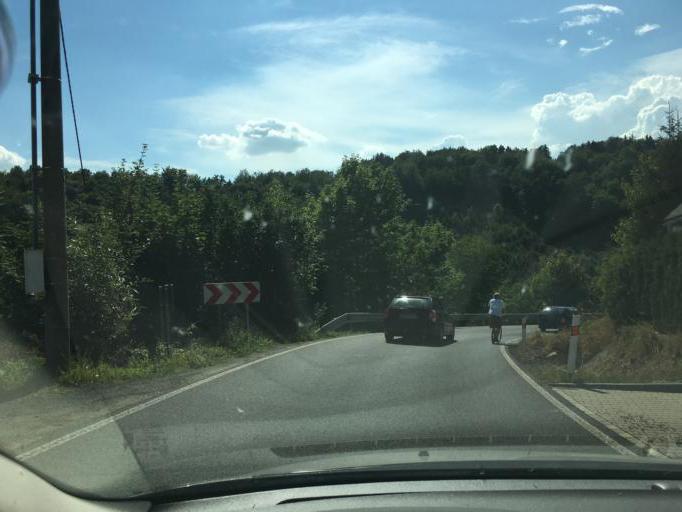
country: CZ
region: Liberecky
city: Mala Skala
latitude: 50.6458
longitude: 15.1762
